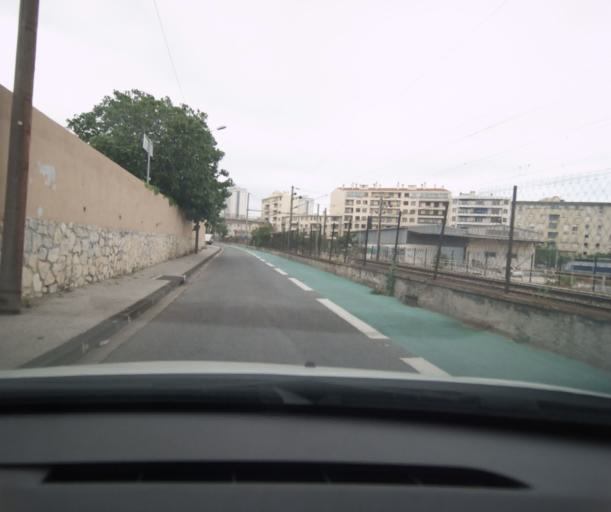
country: FR
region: Provence-Alpes-Cote d'Azur
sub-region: Departement du Var
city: Toulon
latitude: 43.1251
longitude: 5.9395
